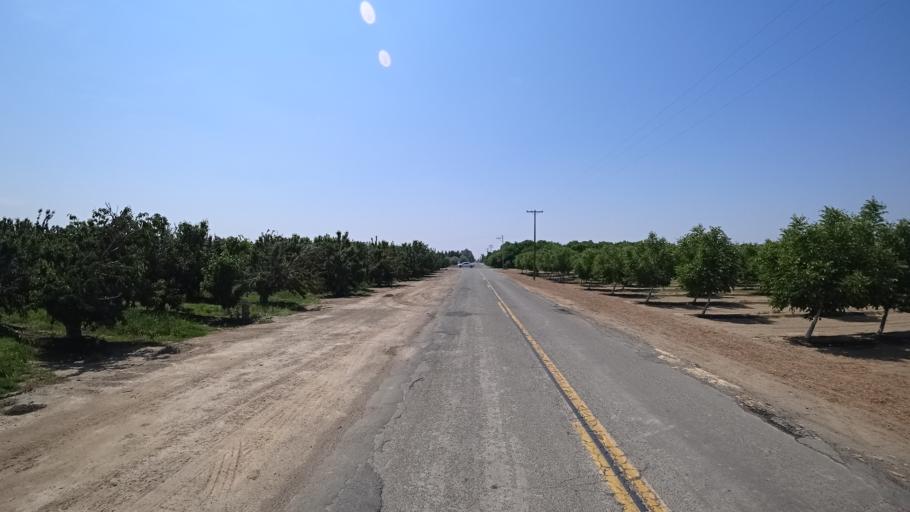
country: US
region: California
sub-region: Kings County
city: Lemoore
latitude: 36.3435
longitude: -119.7628
